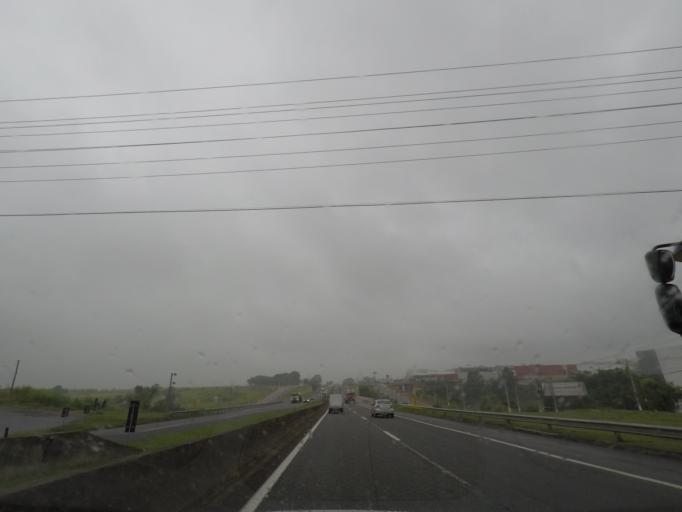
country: BR
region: Sao Paulo
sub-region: Taubate
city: Taubate
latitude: -23.0550
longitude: -45.6113
